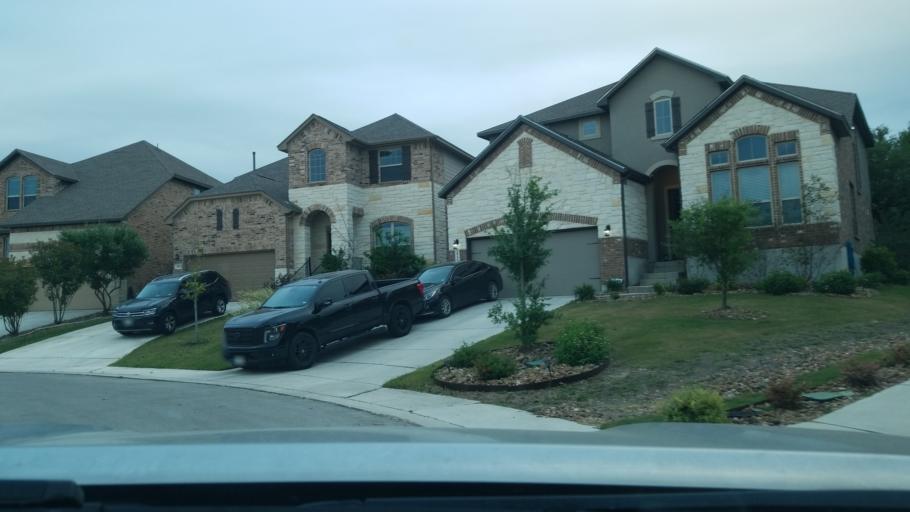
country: US
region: Texas
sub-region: Comal County
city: Bulverde
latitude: 29.7202
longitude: -98.4559
